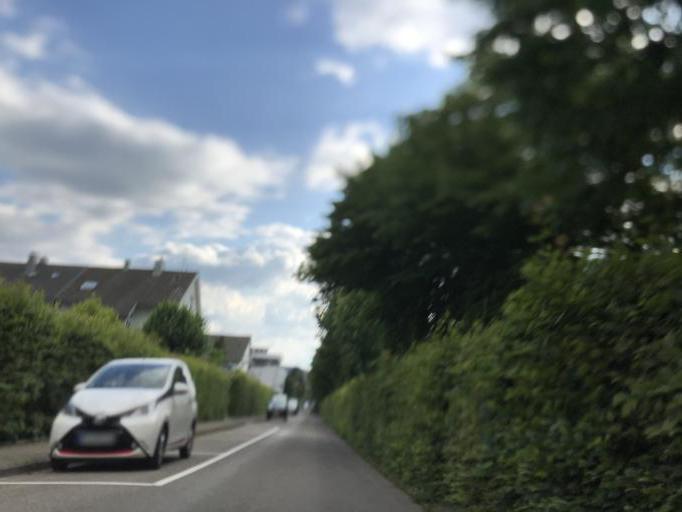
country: DE
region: Baden-Wuerttemberg
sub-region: Freiburg Region
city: Schopfheim
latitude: 47.6522
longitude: 7.8309
